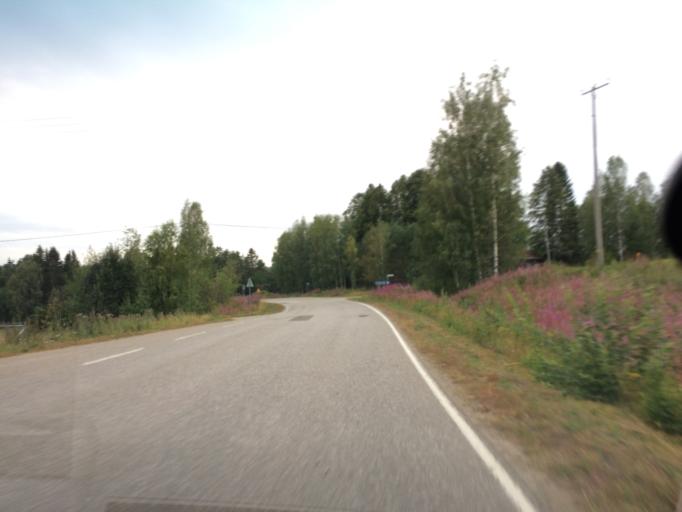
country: FI
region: Pirkanmaa
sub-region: Tampere
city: Luopioinen
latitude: 61.2577
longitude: 24.7101
